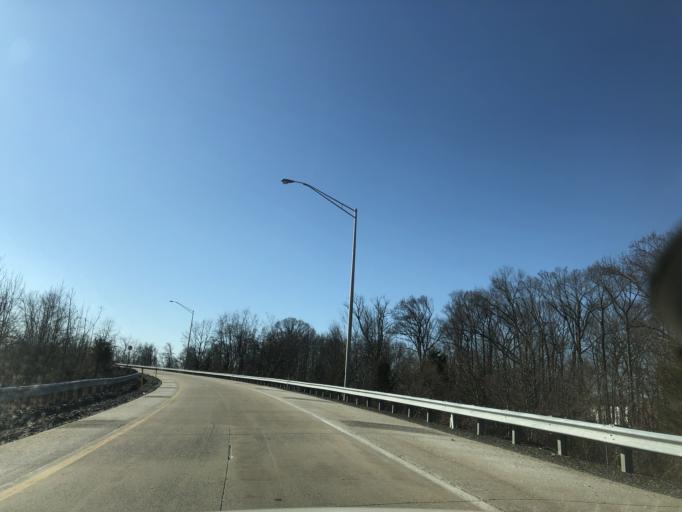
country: US
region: Pennsylvania
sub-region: Bucks County
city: Croydon
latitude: 40.1133
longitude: -74.8932
